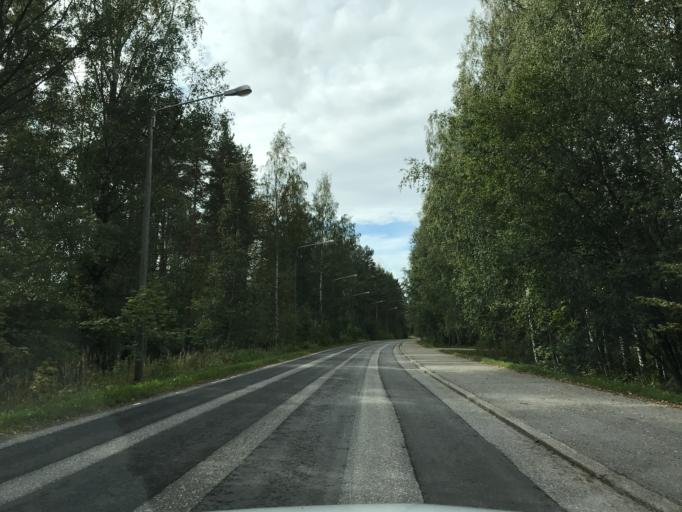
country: FI
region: Paijanne Tavastia
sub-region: Lahti
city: Nastola
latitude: 61.0127
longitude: 25.8107
